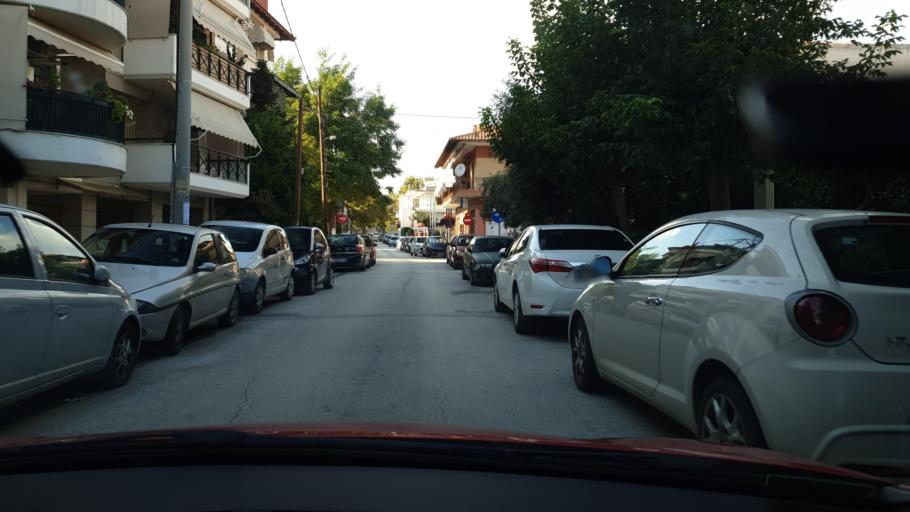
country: GR
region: Central Macedonia
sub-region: Nomos Thessalonikis
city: Thermi
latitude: 40.5454
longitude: 23.0208
